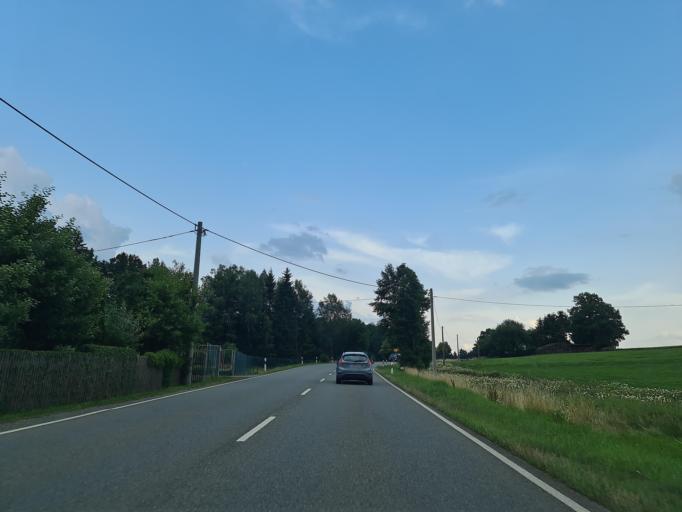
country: DE
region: Saxony
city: Bergen
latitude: 50.4820
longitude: 12.2532
